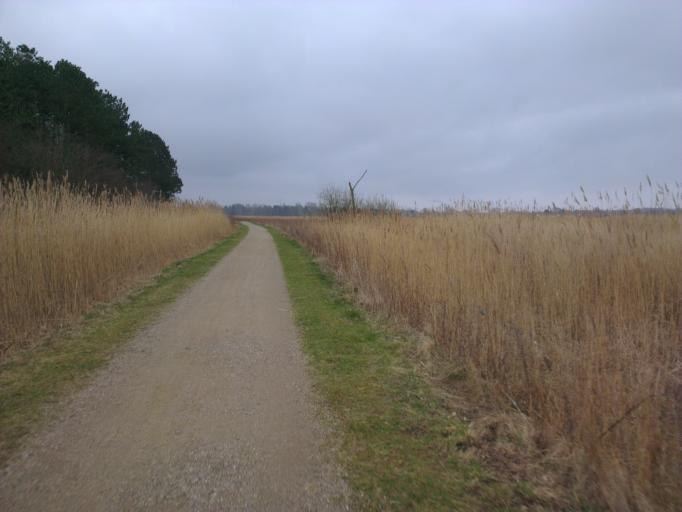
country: DK
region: Capital Region
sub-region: Frederikssund Kommune
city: Frederikssund
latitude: 55.8630
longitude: 12.0679
